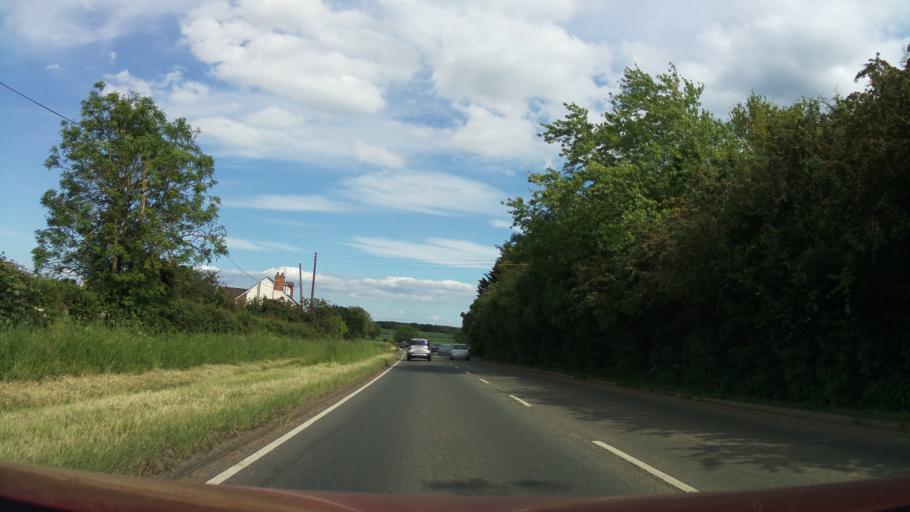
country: GB
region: England
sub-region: Worcestershire
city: Pershore
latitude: 52.1022
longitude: -2.0386
